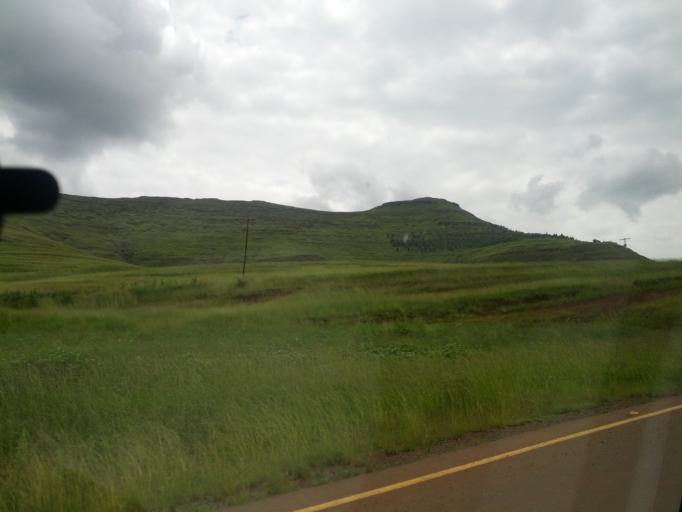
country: LS
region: Leribe
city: Leribe
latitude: -29.0376
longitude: 28.2402
